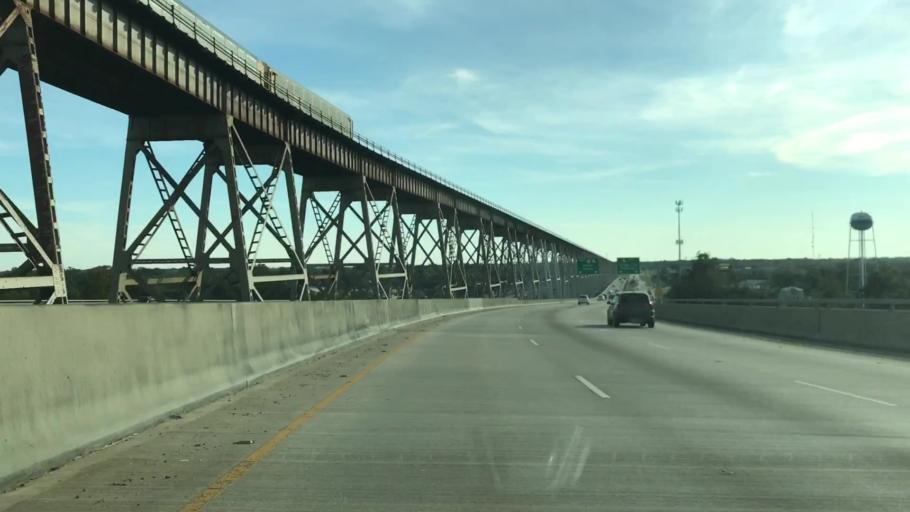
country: US
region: Louisiana
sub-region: Jefferson Parish
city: Bridge City
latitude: 29.9362
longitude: -90.1633
